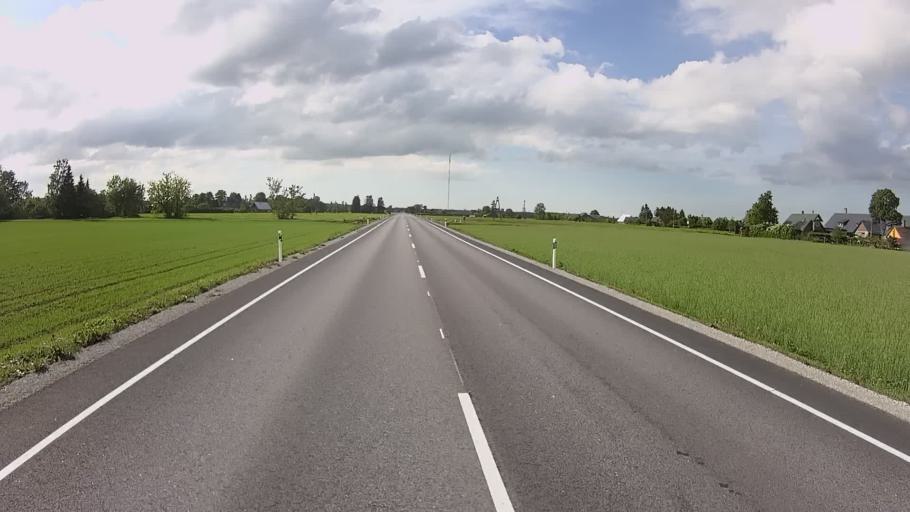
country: EE
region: Laeaene-Virumaa
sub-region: Vinni vald
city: Vinni
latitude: 59.2440
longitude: 26.4820
